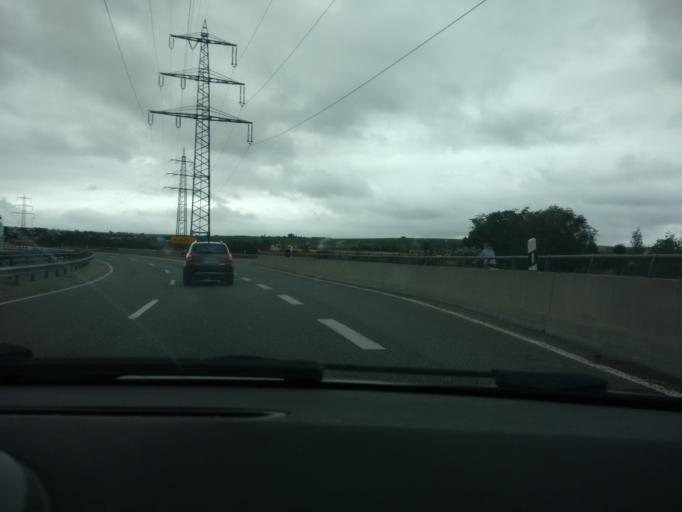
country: DE
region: Rheinland-Pfalz
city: Bretzenheim
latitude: 49.8647
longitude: 7.8866
